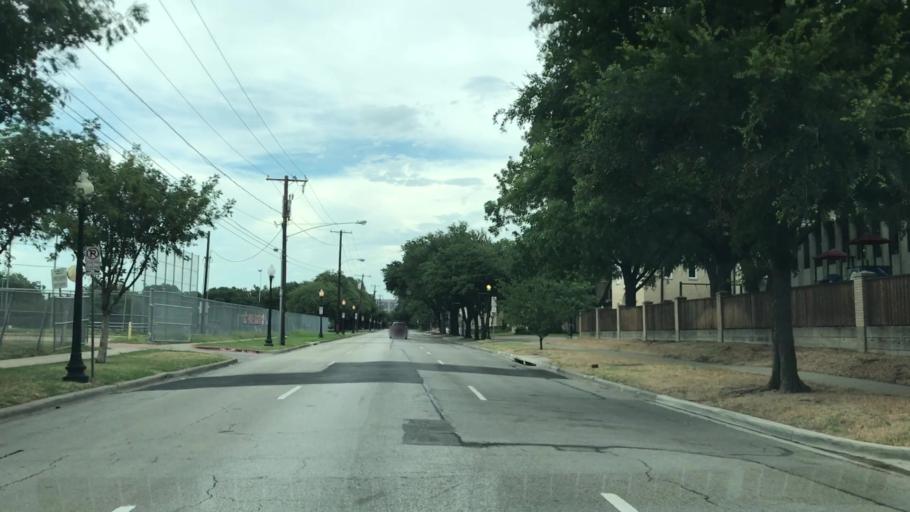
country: US
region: Texas
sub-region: Dallas County
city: Highland Park
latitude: 32.8105
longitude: -96.7939
